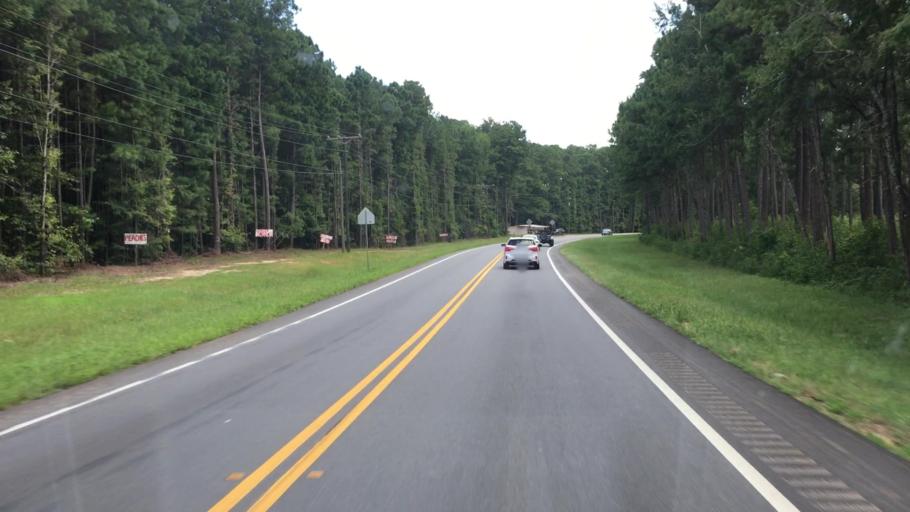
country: US
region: Georgia
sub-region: Putnam County
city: Jefferson
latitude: 33.4077
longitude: -83.3686
